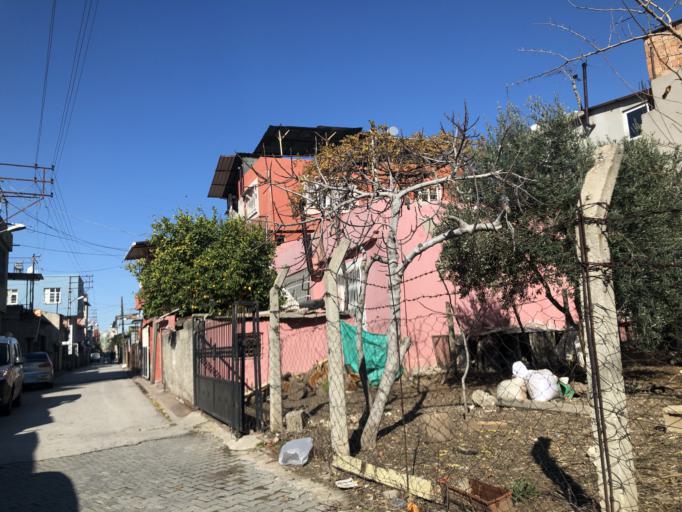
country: TR
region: Adana
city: Yuregir
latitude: 37.0062
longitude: 35.3678
